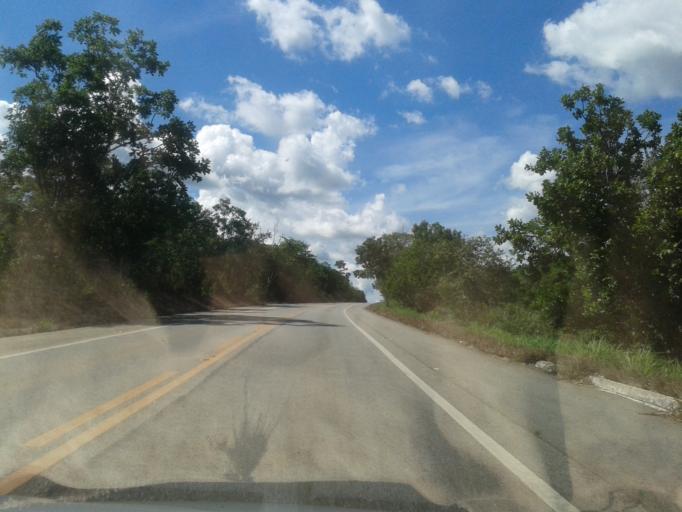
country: BR
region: Goias
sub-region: Itapuranga
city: Itapuranga
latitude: -15.6309
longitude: -50.2314
